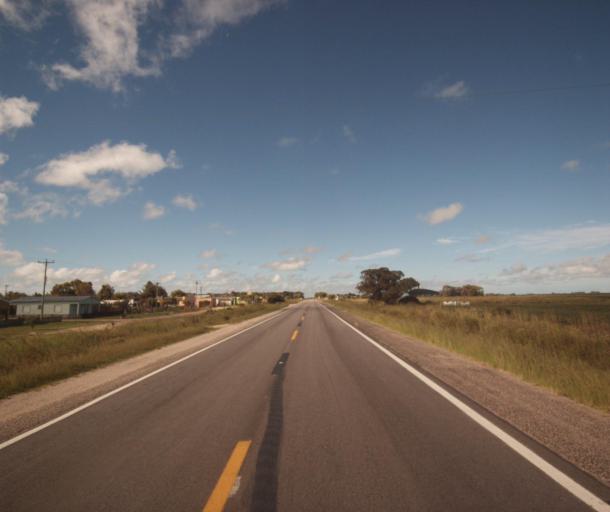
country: UY
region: Cerro Largo
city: Rio Branco
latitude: -32.9439
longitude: -52.7703
